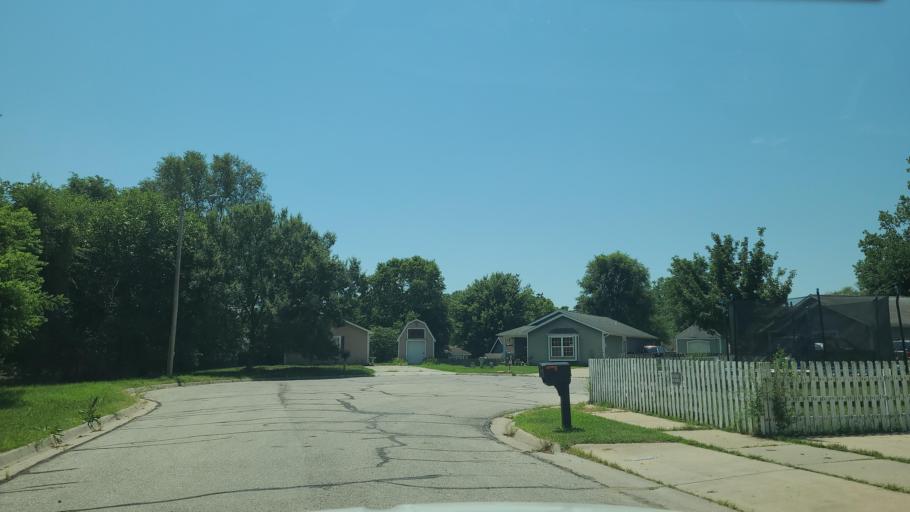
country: US
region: Kansas
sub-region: Douglas County
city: Lawrence
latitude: 38.9743
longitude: -95.2167
